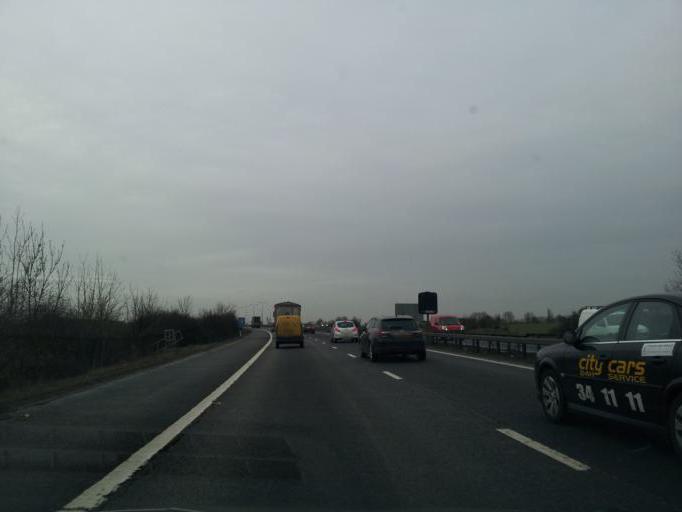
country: GB
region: England
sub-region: Cambridgeshire
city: Girton
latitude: 52.2222
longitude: 0.0784
